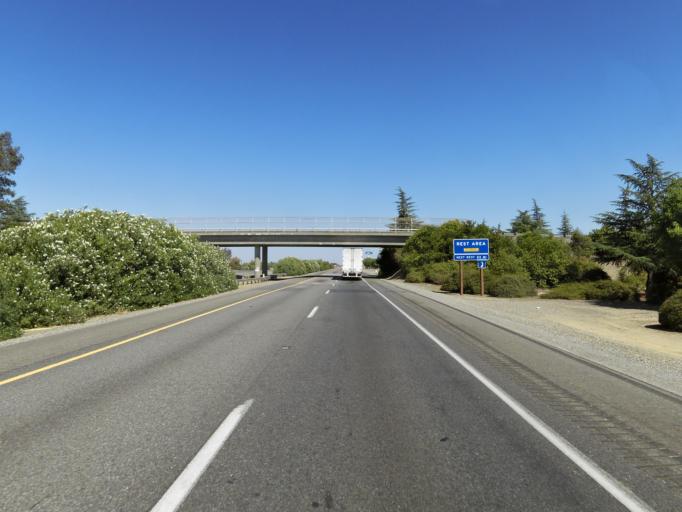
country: US
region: California
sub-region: Tehama County
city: Corning
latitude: 39.9273
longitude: -122.2001
